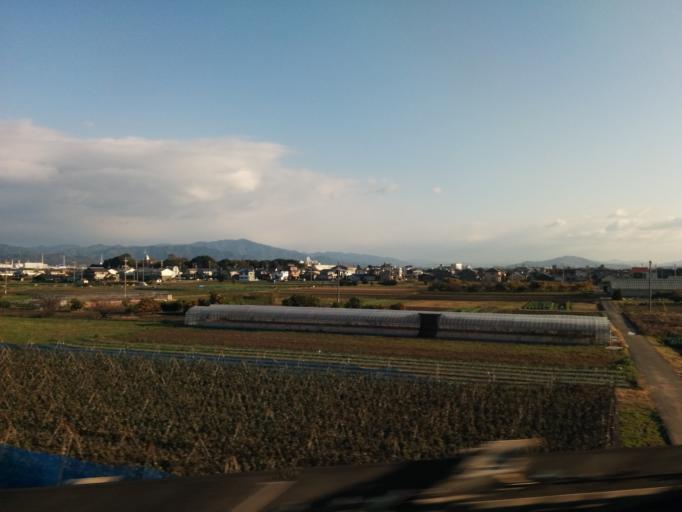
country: JP
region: Aichi
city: Kozakai-cho
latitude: 34.7915
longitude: 137.3447
